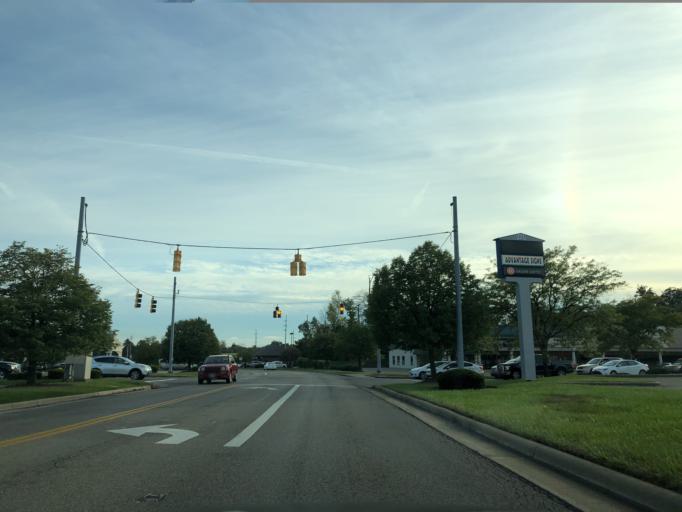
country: US
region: Ohio
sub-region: Hamilton County
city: Sixteen Mile Stand
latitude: 39.2903
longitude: -84.3051
